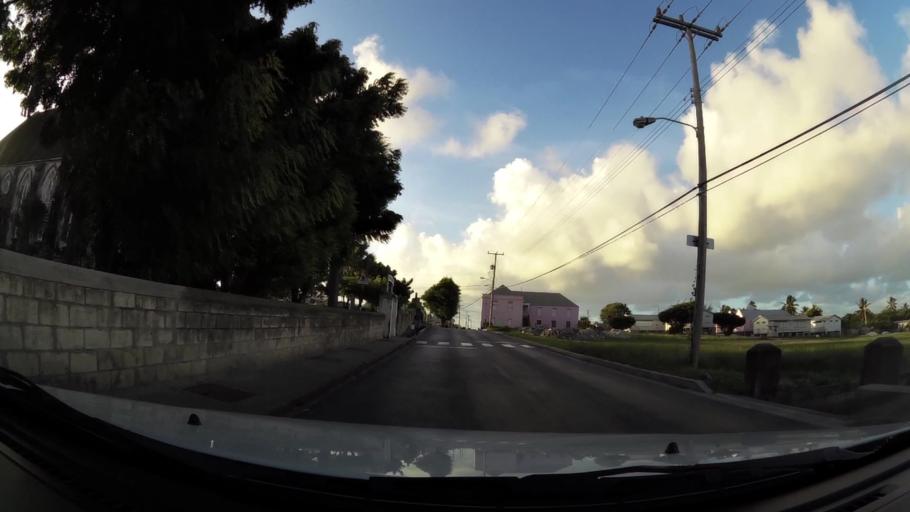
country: BB
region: Saint Philip
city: Crane
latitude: 13.0957
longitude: -59.4657
